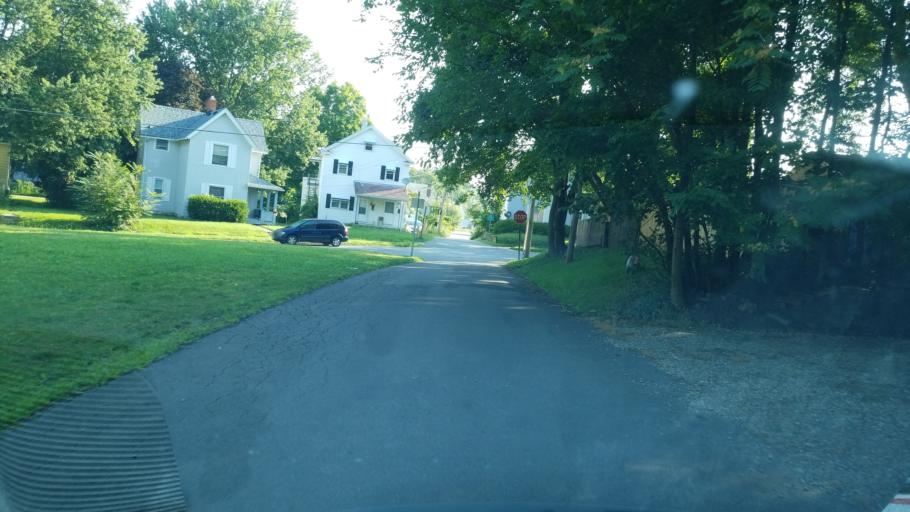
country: US
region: Ohio
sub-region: Richland County
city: Mansfield
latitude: 40.7497
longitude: -82.5202
